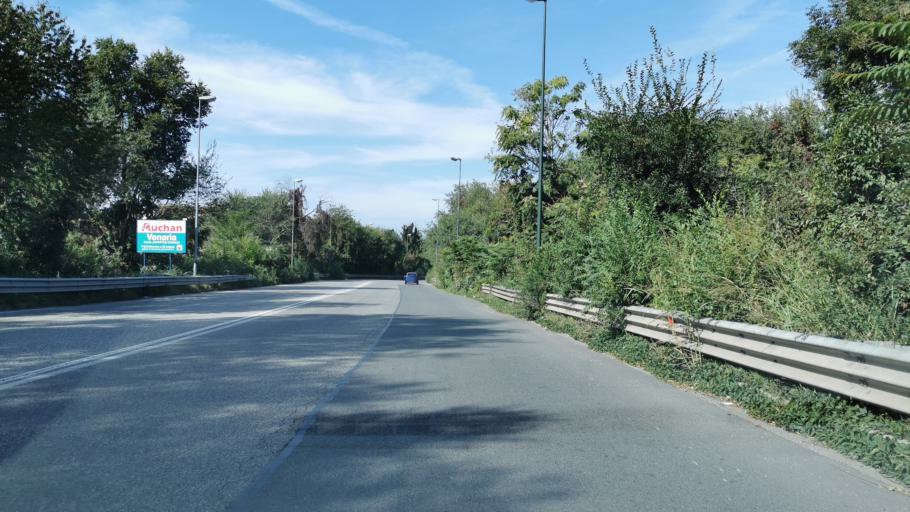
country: IT
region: Piedmont
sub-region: Provincia di Torino
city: Venaria Reale
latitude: 45.1166
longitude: 7.6617
